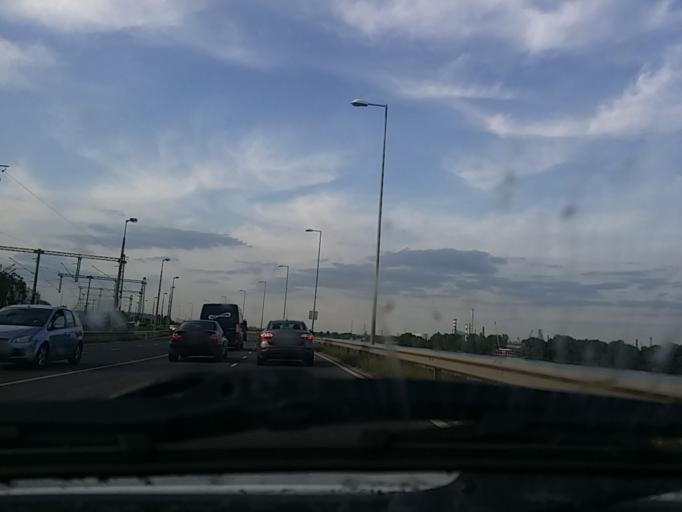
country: HU
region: Budapest
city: Budapest XXII. keruelet
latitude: 47.4160
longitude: 19.0420
